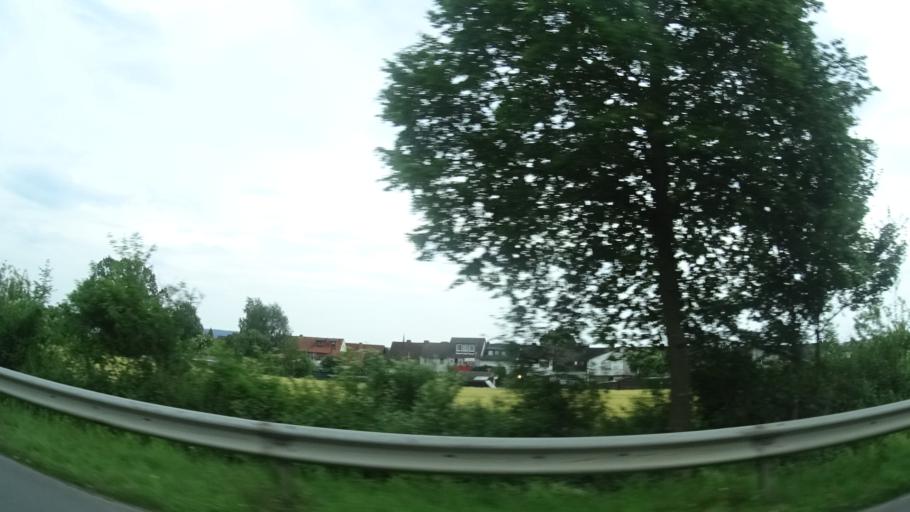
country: DE
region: North Rhine-Westphalia
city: Brakel
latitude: 51.7167
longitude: 9.1675
